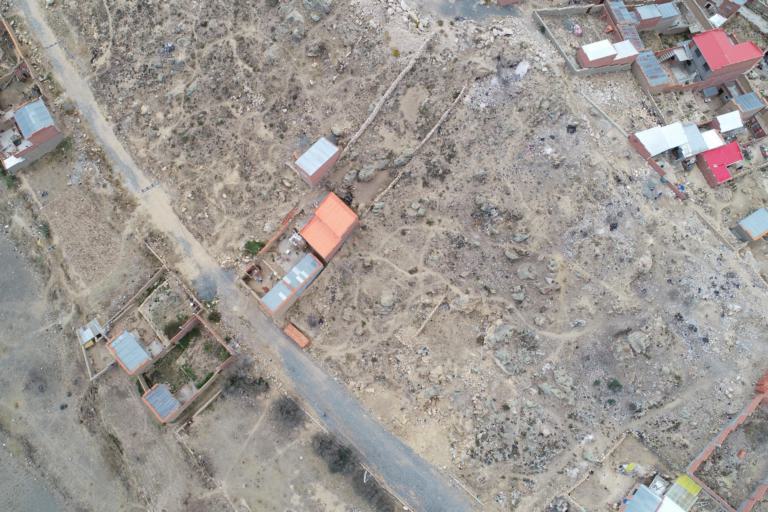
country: BO
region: La Paz
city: Achacachi
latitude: -16.0415
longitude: -68.6816
